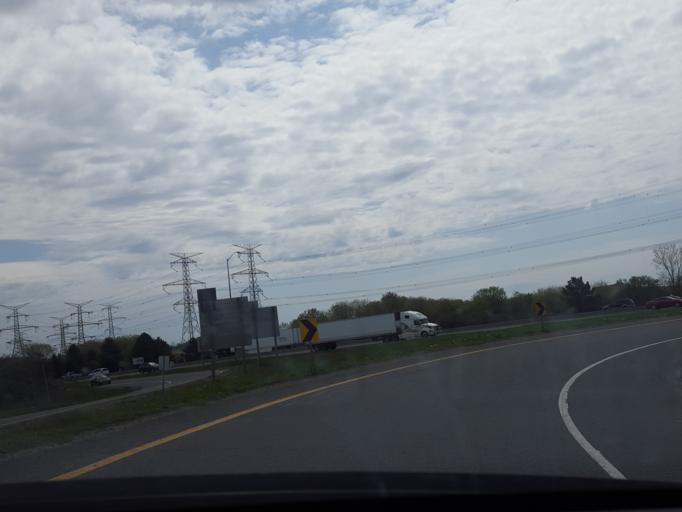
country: CA
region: Ontario
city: Oshawa
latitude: 43.8959
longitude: -78.6889
